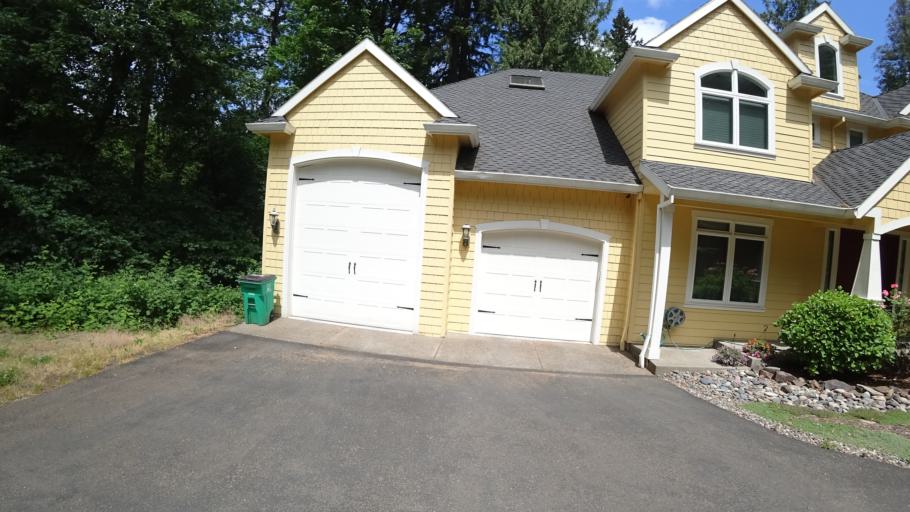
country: US
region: Oregon
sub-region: Clackamas County
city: Lake Oswego
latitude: 45.4445
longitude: -122.6908
